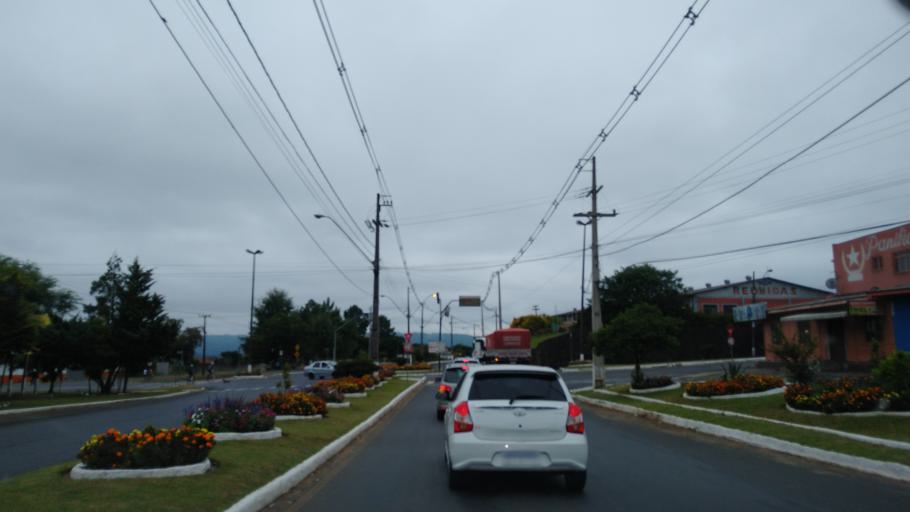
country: BR
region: Santa Catarina
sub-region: Porto Uniao
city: Porto Uniao
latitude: -26.2503
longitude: -51.0834
